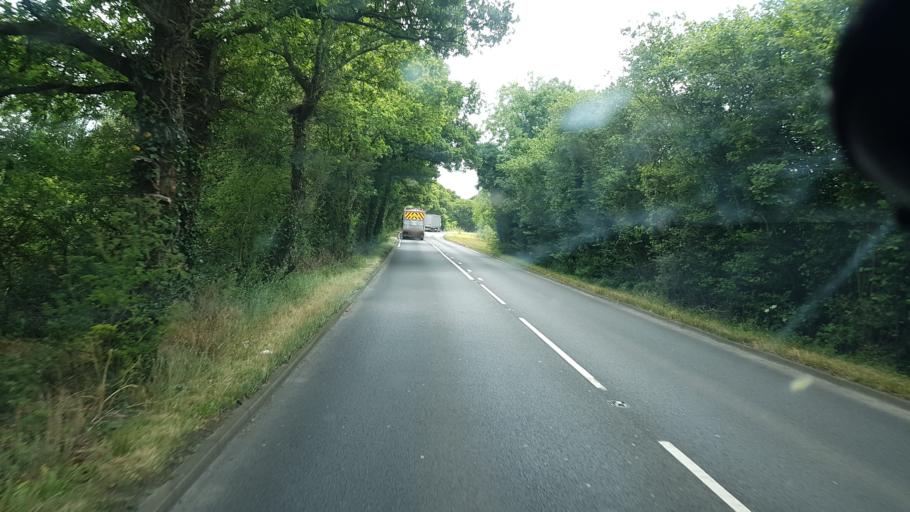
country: GB
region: England
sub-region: Surrey
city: Lingfield
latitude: 51.1808
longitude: -0.0470
